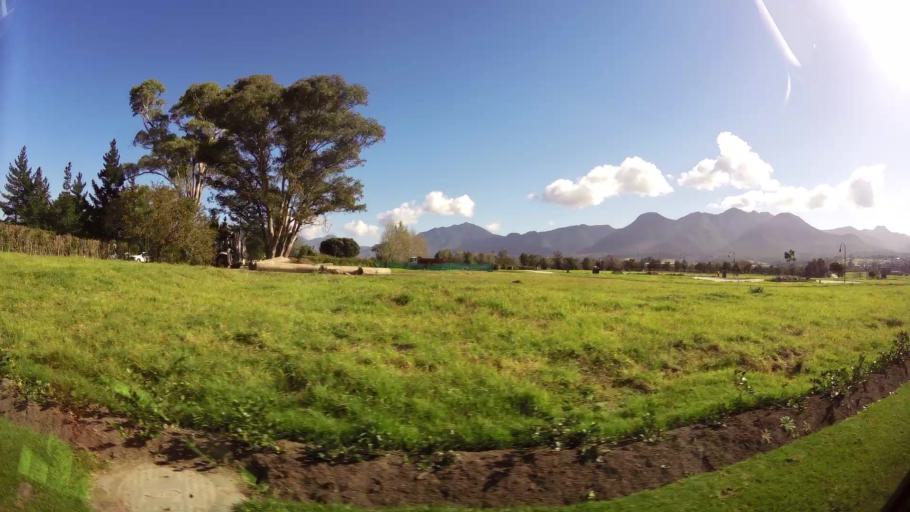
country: ZA
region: Western Cape
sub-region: Eden District Municipality
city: George
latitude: -33.9629
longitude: 22.4015
